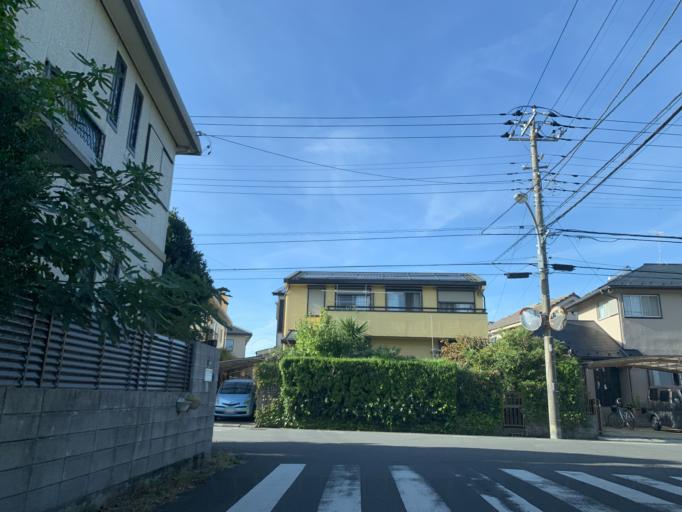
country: JP
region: Chiba
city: Nagareyama
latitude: 35.8963
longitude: 139.9286
